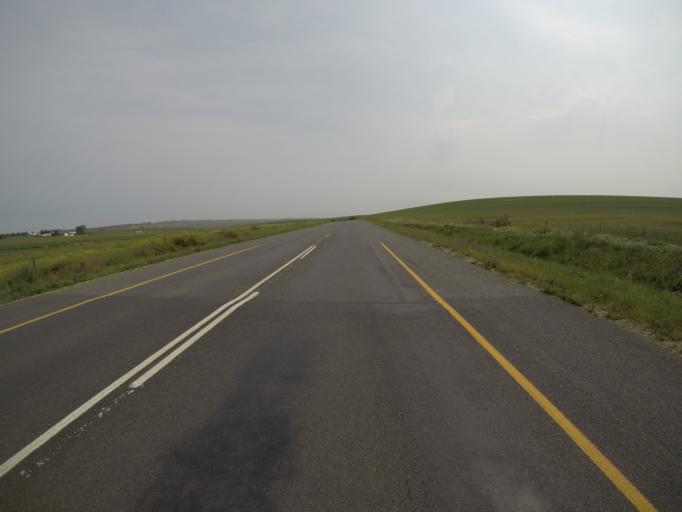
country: ZA
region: Western Cape
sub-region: West Coast District Municipality
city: Malmesbury
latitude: -33.4566
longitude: 18.7829
